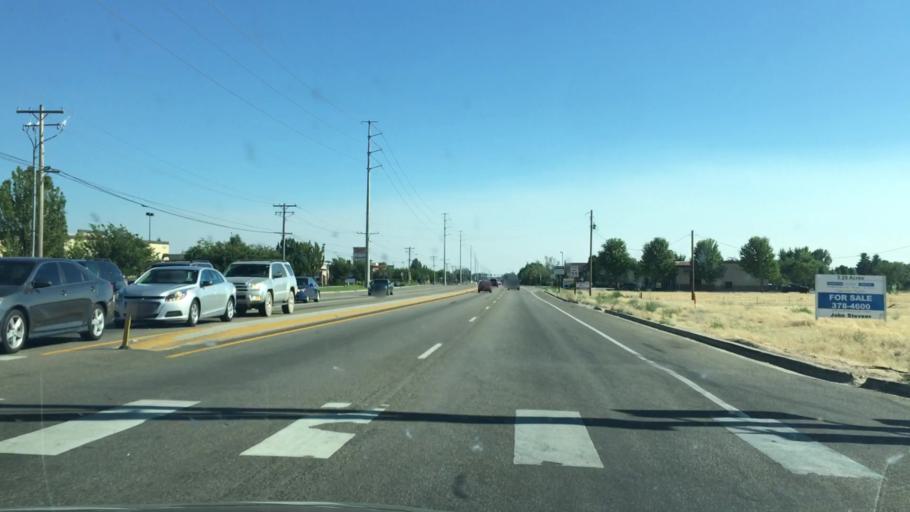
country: US
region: Idaho
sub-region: Ada County
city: Meridian
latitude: 43.6336
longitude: -116.3545
